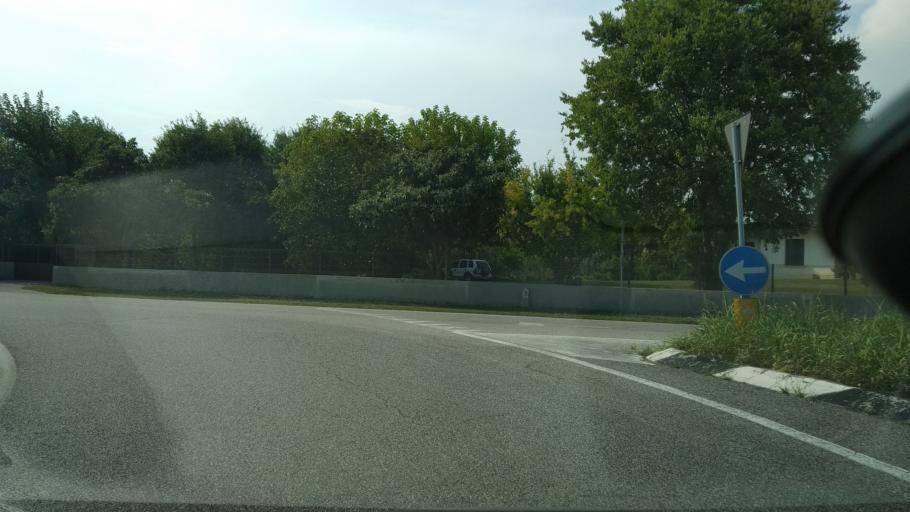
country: IT
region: Veneto
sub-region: Provincia di Padova
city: Cittadella
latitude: 45.6551
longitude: 11.7896
